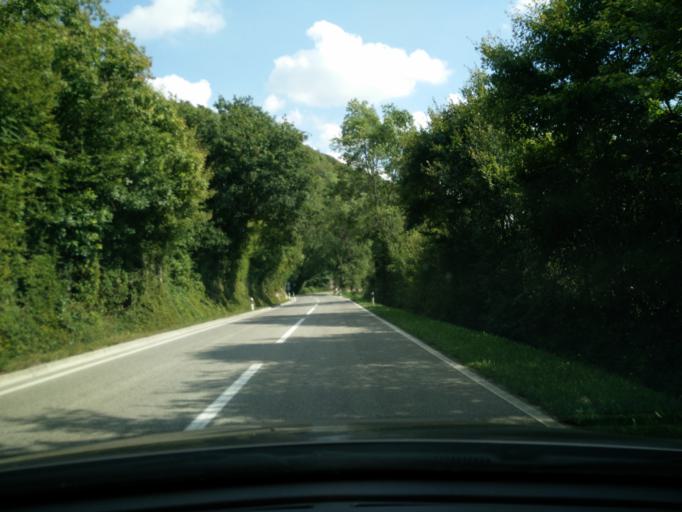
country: HR
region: Istarska
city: Buzet
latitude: 45.3934
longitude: 13.9120
